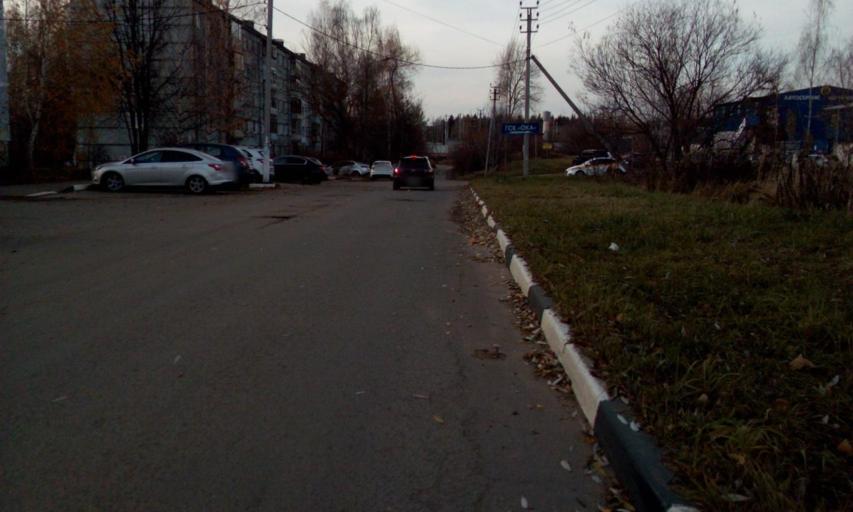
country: RU
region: Moskovskaya
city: Aprelevka
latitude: 55.5547
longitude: 37.0861
